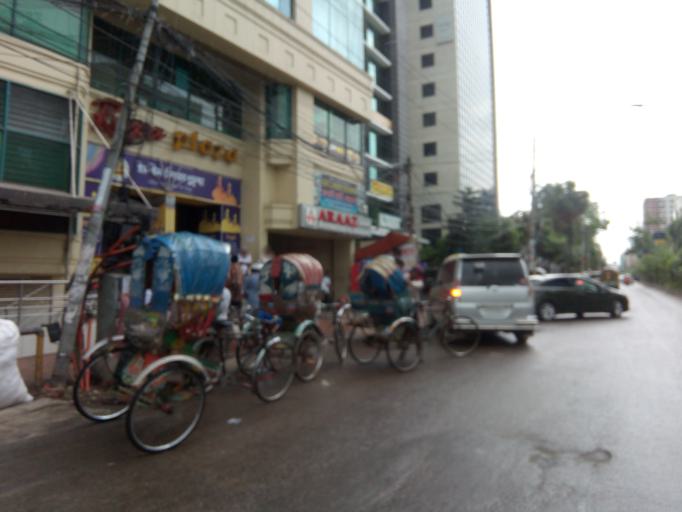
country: BD
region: Dhaka
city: Azimpur
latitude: 23.7563
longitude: 90.3750
